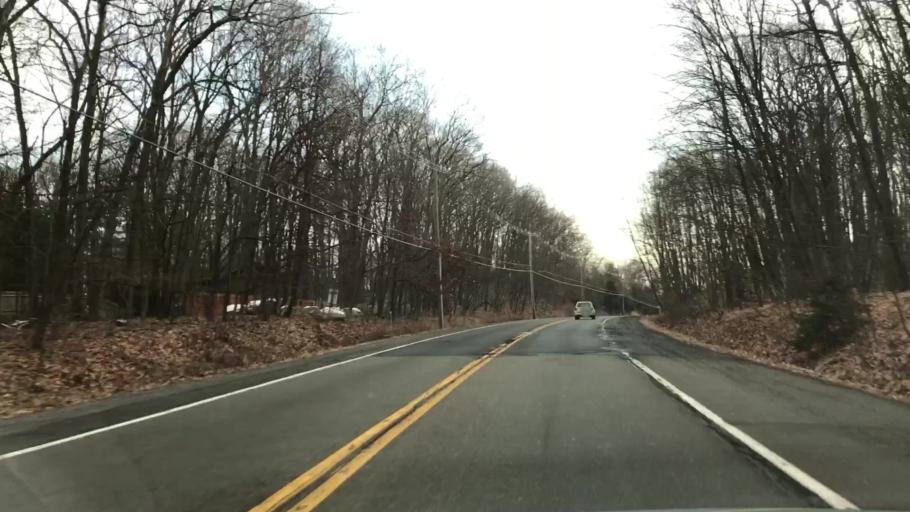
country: US
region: New York
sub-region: Rockland County
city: Wesley Hills
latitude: 41.1834
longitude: -74.0656
